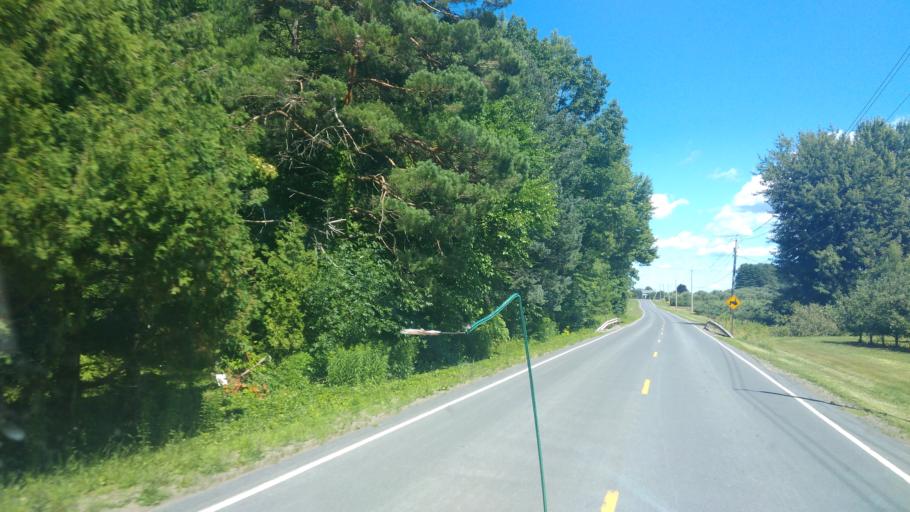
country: US
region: New York
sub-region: Wayne County
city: Sodus
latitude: 43.1817
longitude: -77.0289
